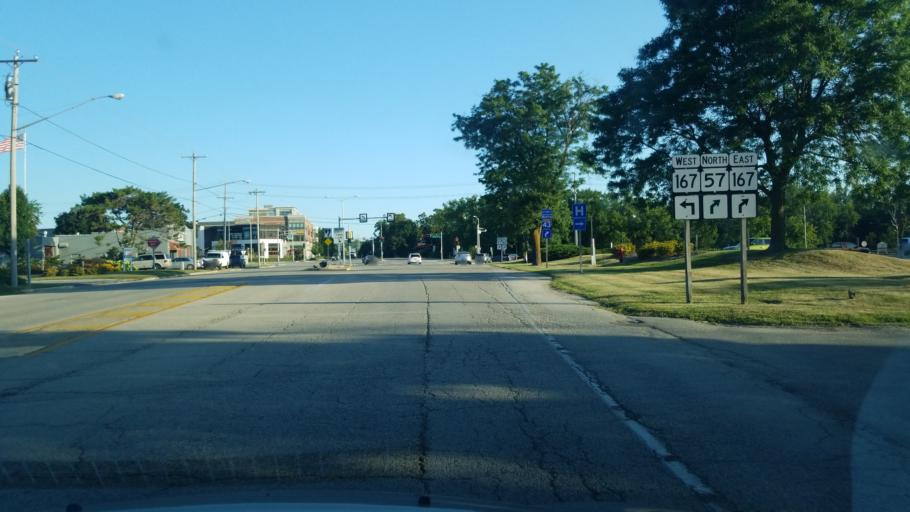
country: US
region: Wisconsin
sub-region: Ozaukee County
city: Mequon
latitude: 43.2204
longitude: -87.9819
